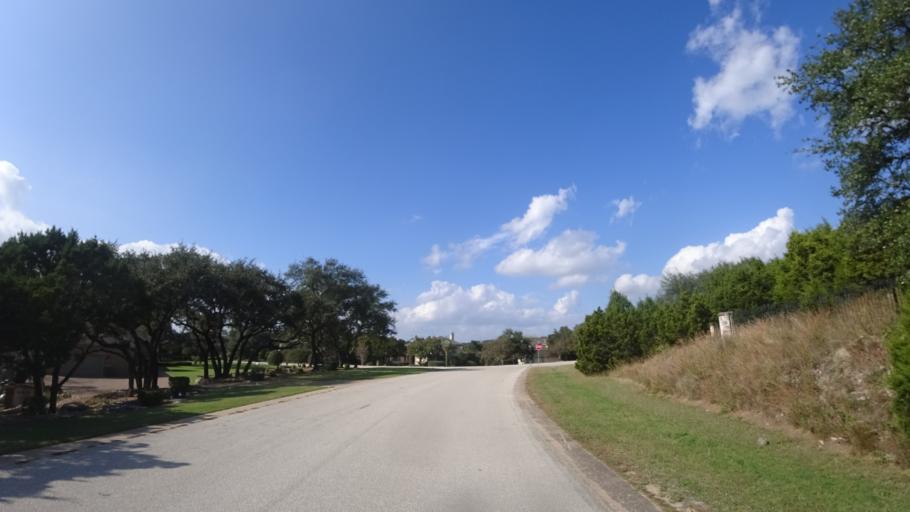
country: US
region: Texas
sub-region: Travis County
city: Lost Creek
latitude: 30.3079
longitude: -97.8552
